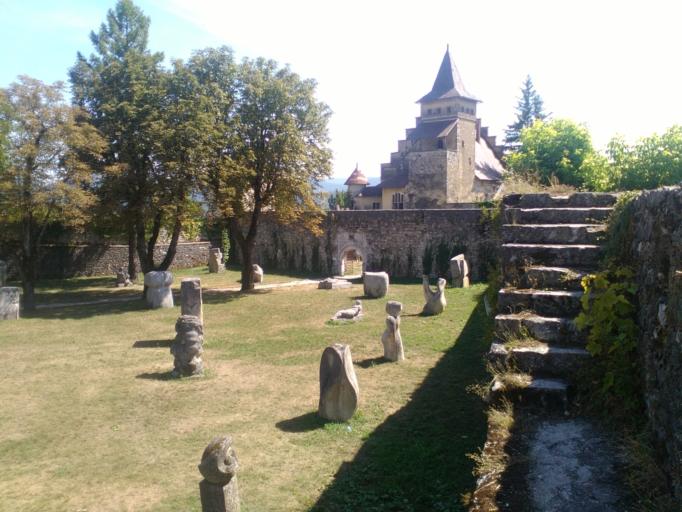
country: BA
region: Federation of Bosnia and Herzegovina
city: Ostrozac
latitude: 44.9050
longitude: 15.9364
